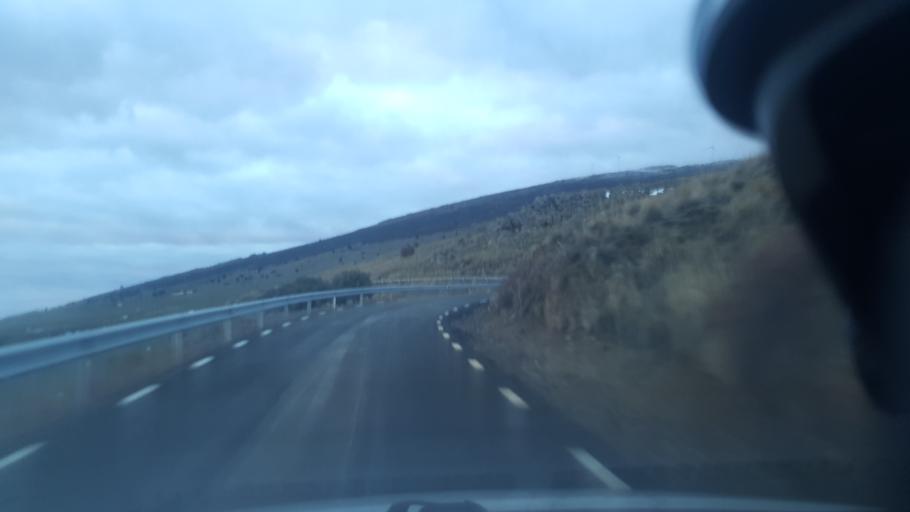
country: ES
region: Castille and Leon
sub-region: Provincia de Avila
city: Ojos-Albos
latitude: 40.7011
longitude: -4.4422
